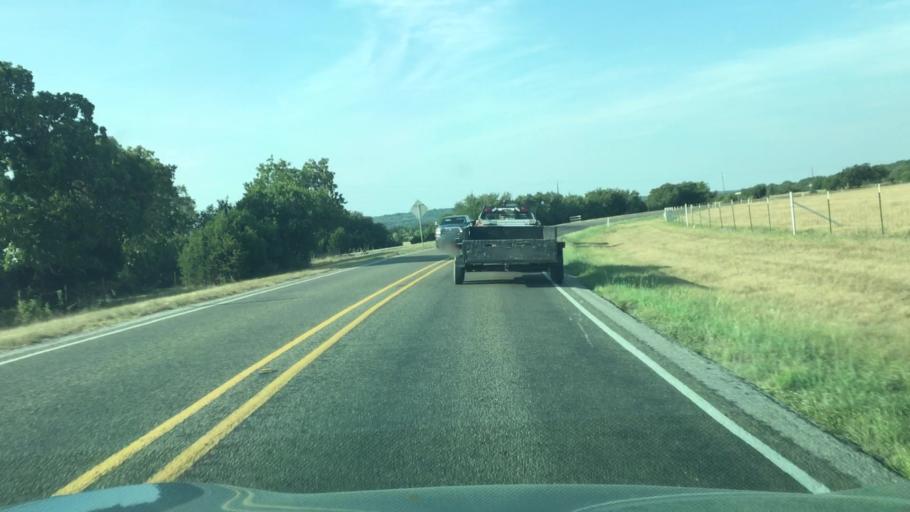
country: US
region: Texas
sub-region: Hays County
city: Dripping Springs
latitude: 30.1895
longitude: -98.2150
